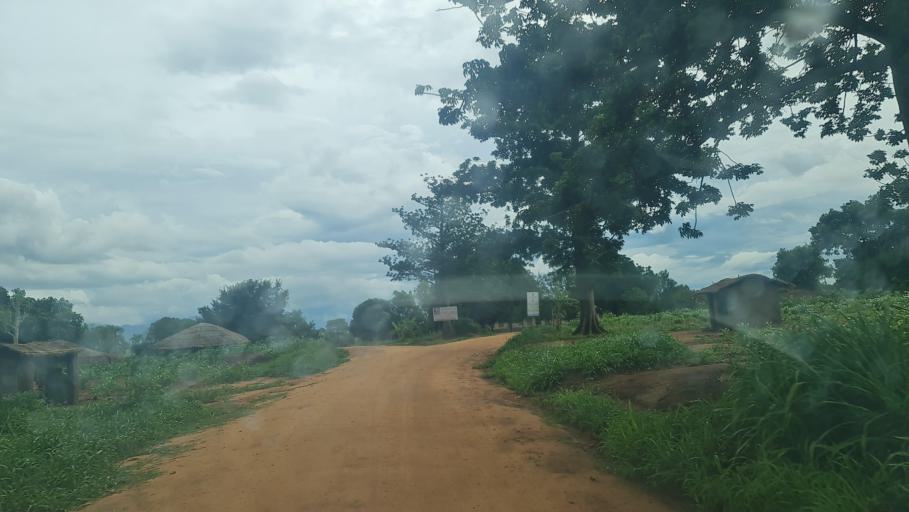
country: MW
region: Southern Region
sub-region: Nsanje District
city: Nsanje
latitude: -17.3954
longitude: 35.5735
